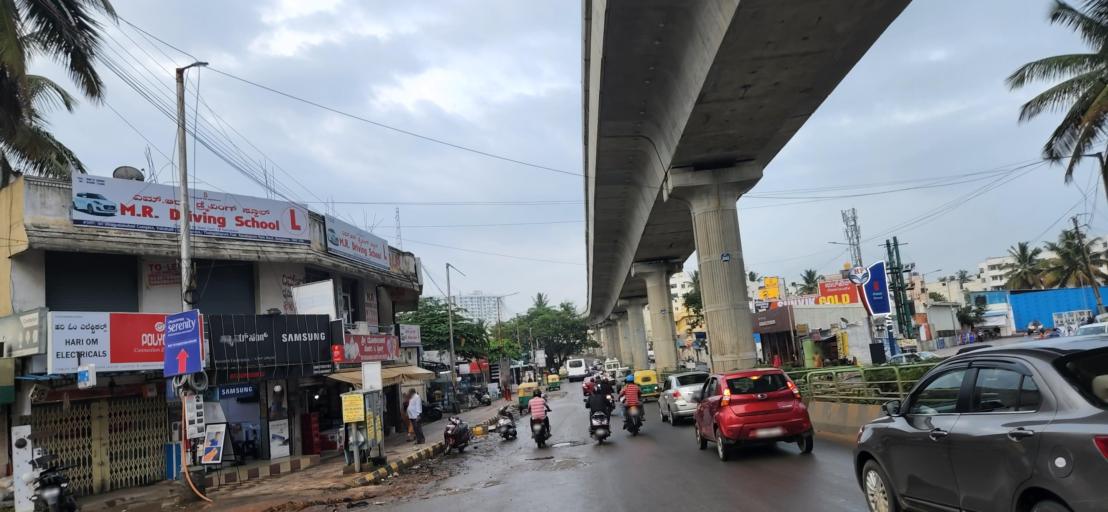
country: IN
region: Karnataka
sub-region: Bangalore Urban
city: Bangalore
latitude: 12.8741
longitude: 77.5408
